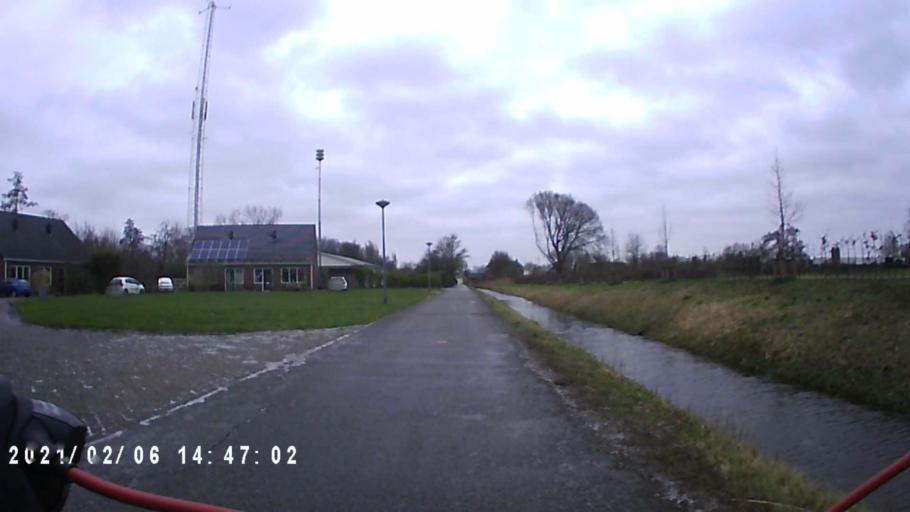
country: NL
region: Groningen
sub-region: Gemeente Winsum
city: Winsum
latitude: 53.3935
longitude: 6.5573
